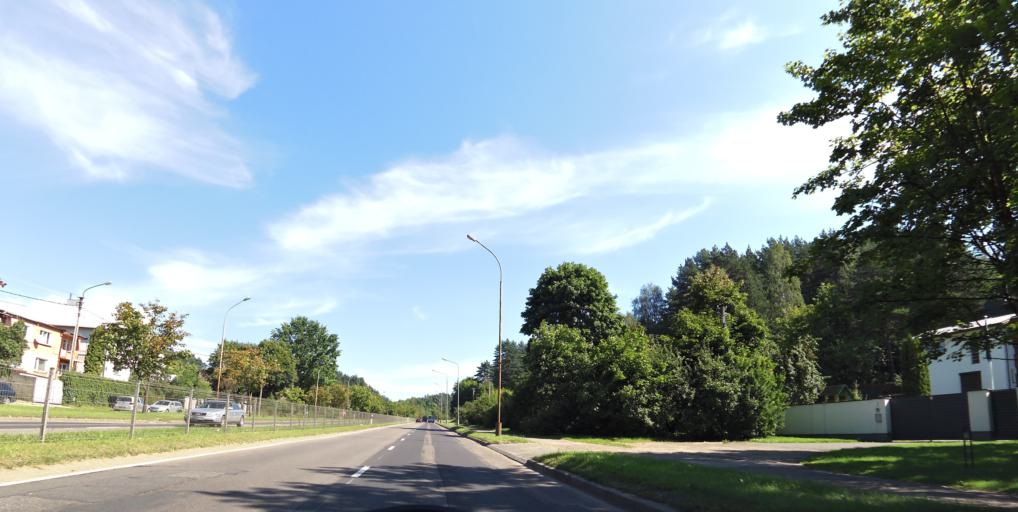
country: LT
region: Vilnius County
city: Rasos
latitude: 54.6869
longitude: 25.3260
